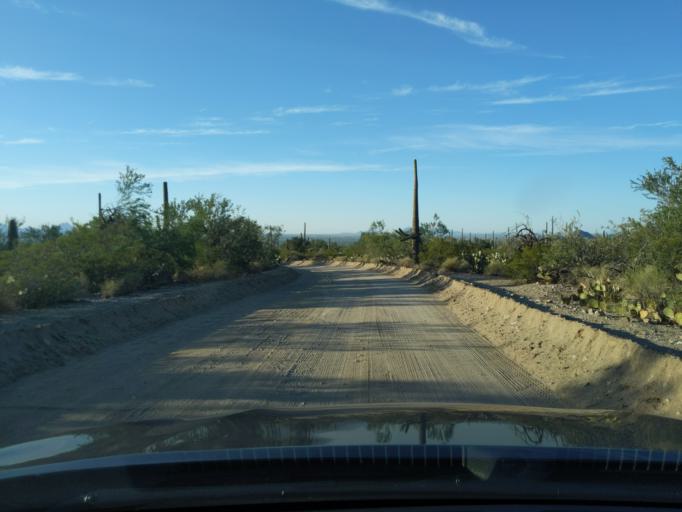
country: US
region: Arizona
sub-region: Pima County
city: Picture Rocks
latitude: 32.2862
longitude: -111.1877
